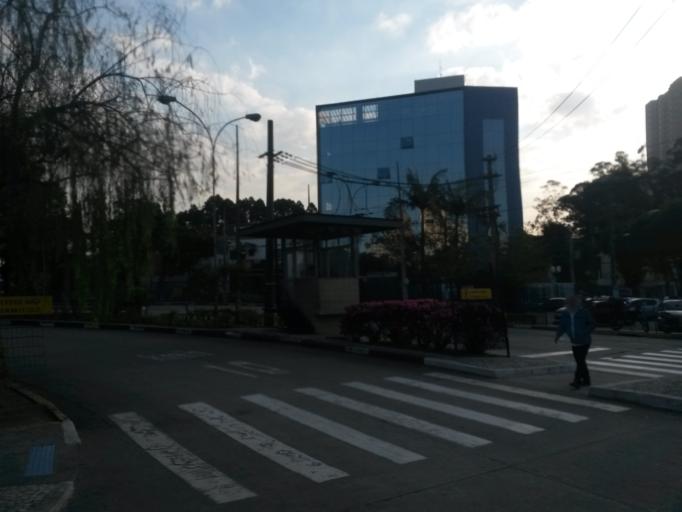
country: BR
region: Sao Paulo
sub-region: Sao Bernardo Do Campo
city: Sao Bernardo do Campo
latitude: -23.7196
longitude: -46.5510
